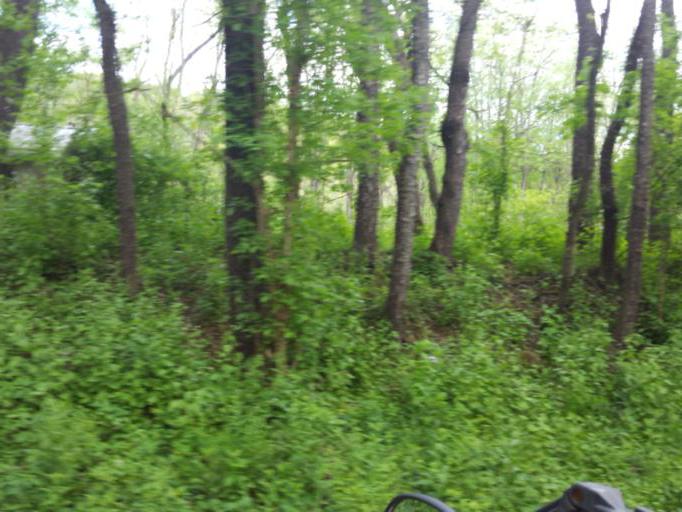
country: US
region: Ohio
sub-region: Ashland County
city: Loudonville
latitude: 40.5515
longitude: -82.1996
